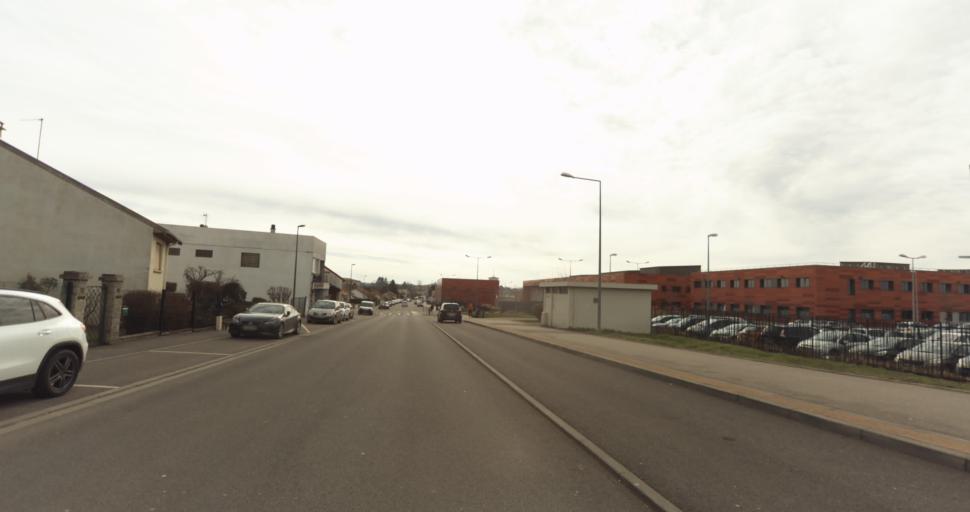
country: FR
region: Lorraine
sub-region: Departement de Meurthe-et-Moselle
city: Jarny
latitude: 49.1587
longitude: 5.8760
